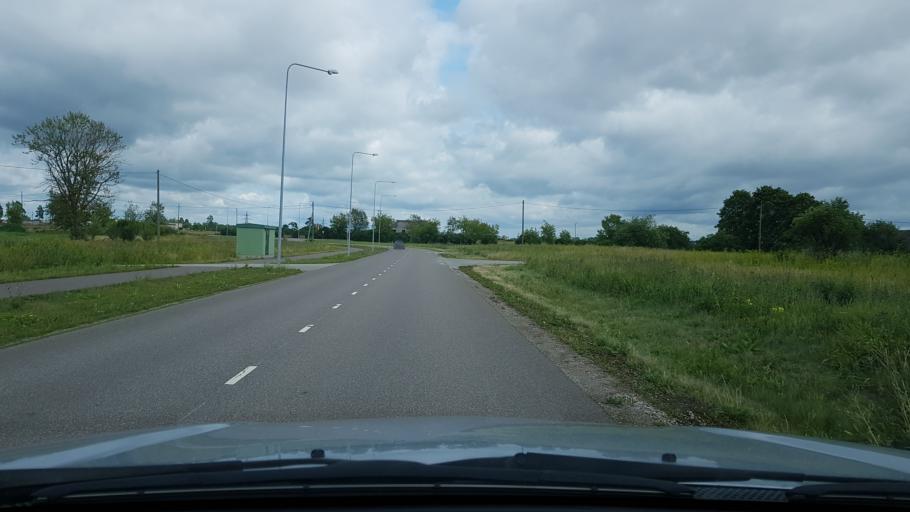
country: EE
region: Ida-Virumaa
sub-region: Narva linn
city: Narva
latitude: 59.3907
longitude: 28.1262
